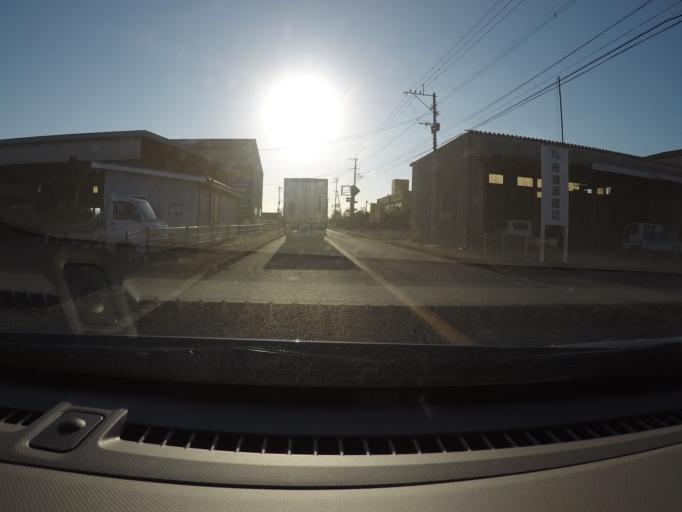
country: JP
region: Kagoshima
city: Izumi
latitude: 32.0902
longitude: 130.2893
